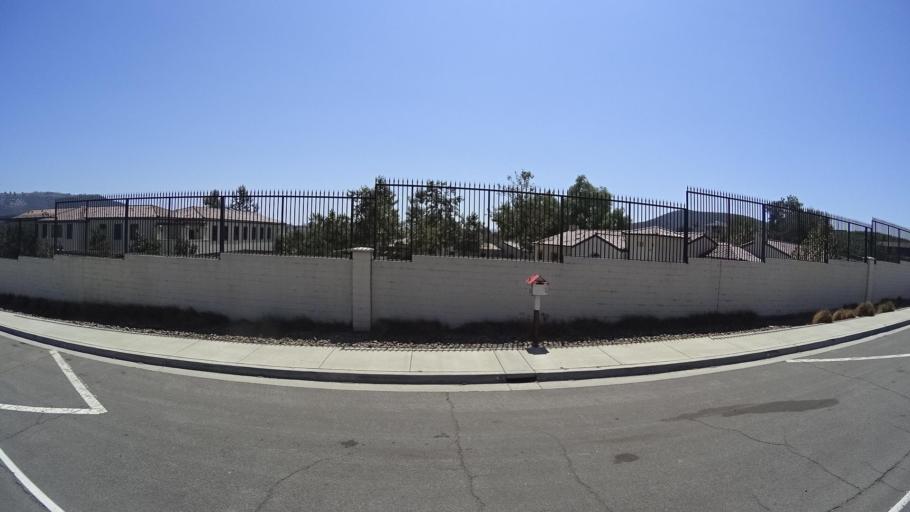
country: US
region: California
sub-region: San Diego County
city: San Marcos
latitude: 33.1830
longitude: -117.1606
